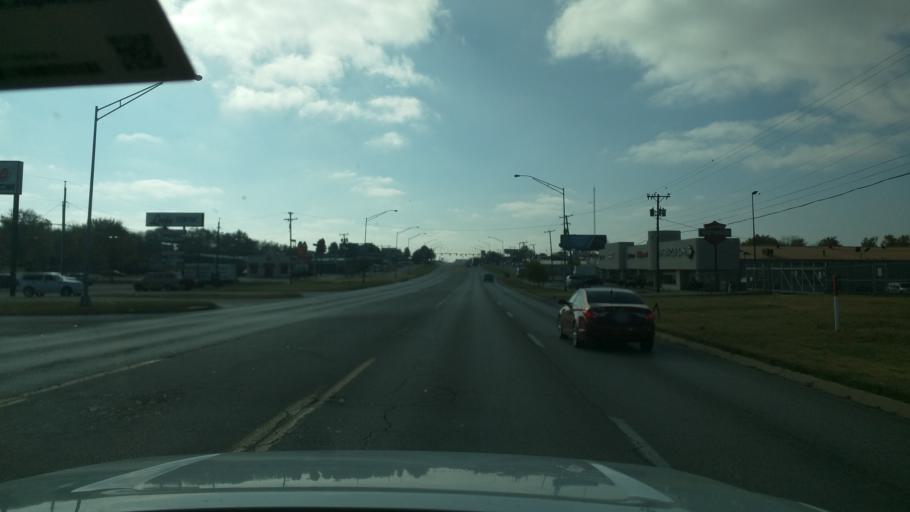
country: US
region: Oklahoma
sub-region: Washington County
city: Dewey
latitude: 36.7609
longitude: -95.9355
